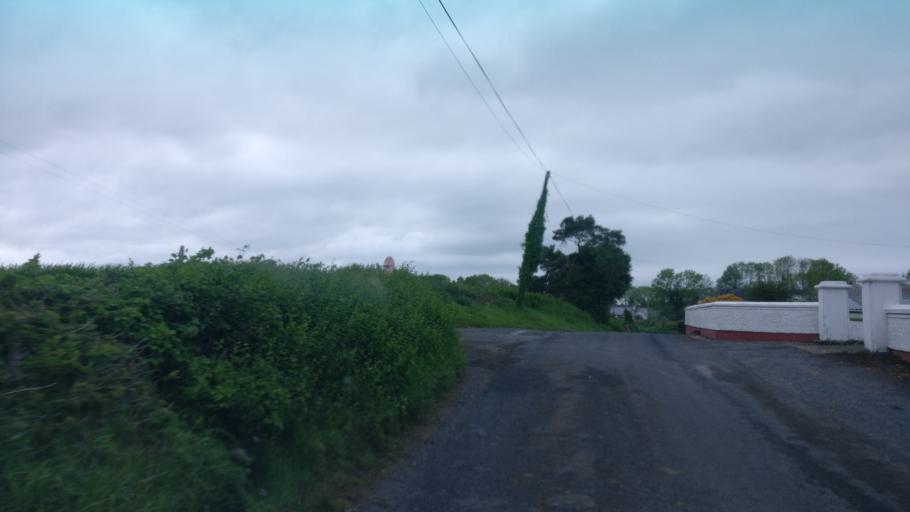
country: IE
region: Connaught
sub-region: County Galway
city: Portumna
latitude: 53.1175
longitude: -8.2895
